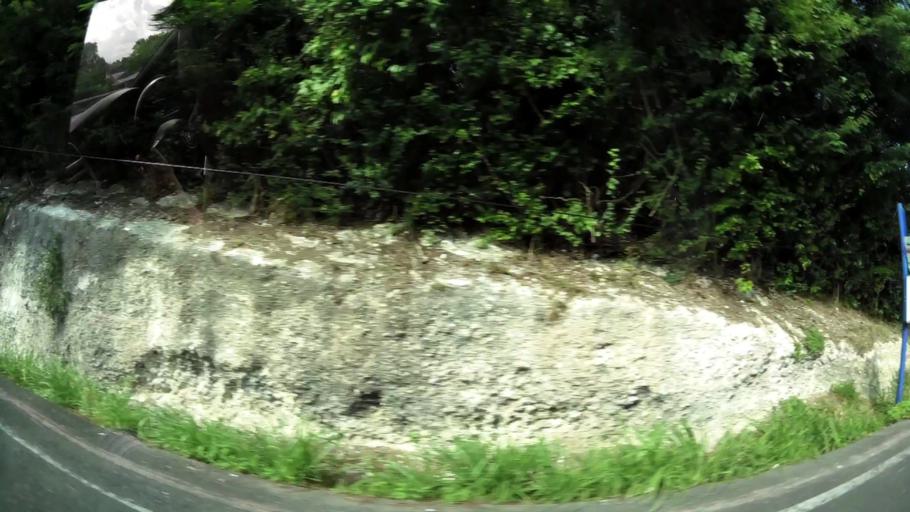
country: GP
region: Guadeloupe
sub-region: Guadeloupe
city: Le Gosier
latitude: 16.2081
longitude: -61.4500
